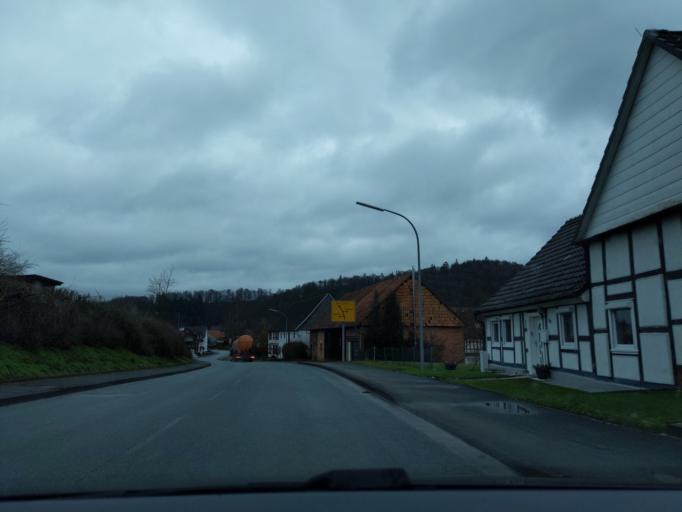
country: DE
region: Hesse
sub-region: Regierungsbezirk Kassel
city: Sachsenhausen
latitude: 51.3058
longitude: 9.0069
